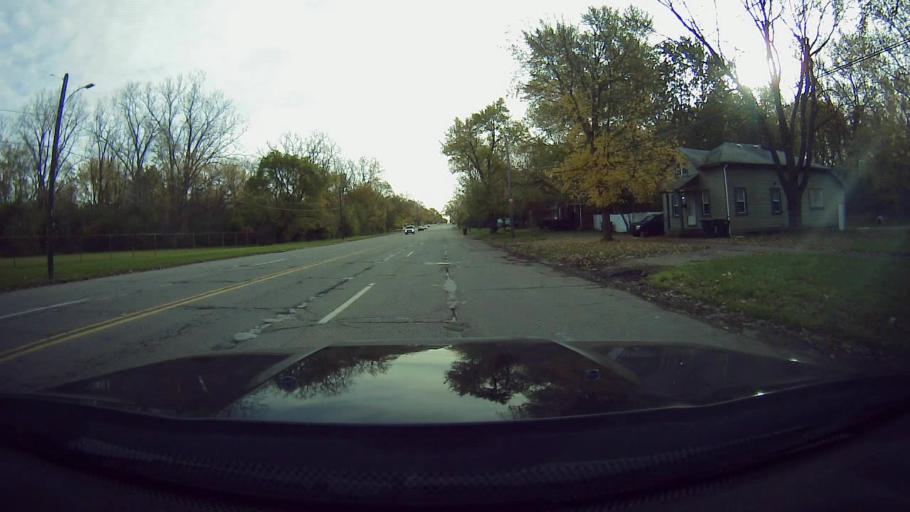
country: US
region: Michigan
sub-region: Wayne County
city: Redford
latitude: 42.4147
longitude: -83.2695
